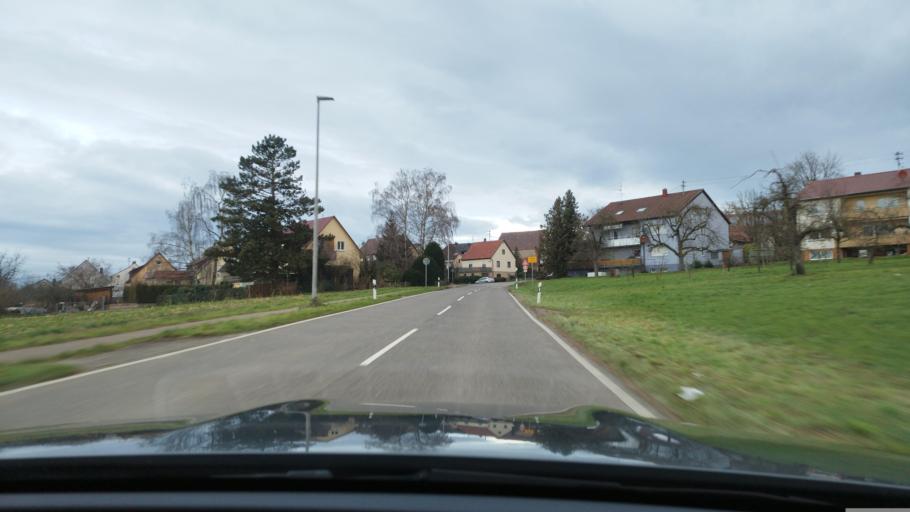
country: DE
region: Baden-Wuerttemberg
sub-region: Regierungsbezirk Stuttgart
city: Burgstetten
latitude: 48.9242
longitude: 9.3911
